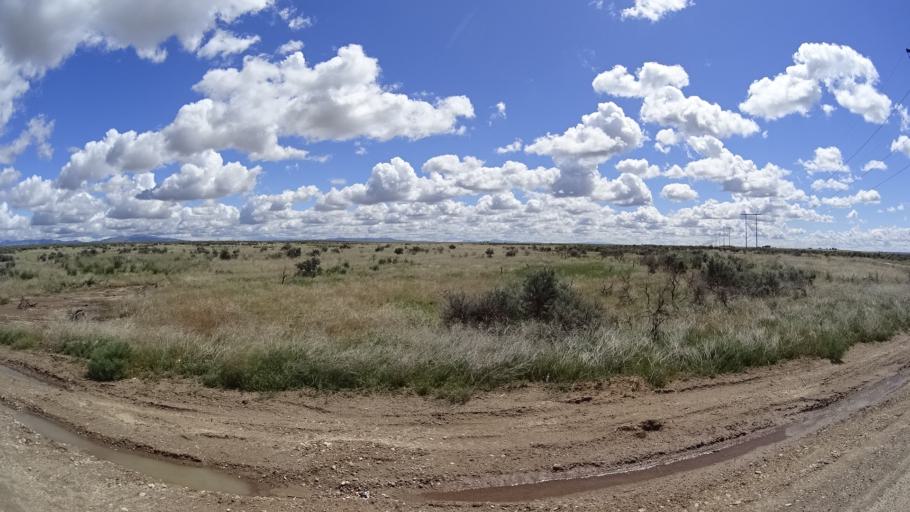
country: US
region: Idaho
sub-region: Ada County
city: Kuna
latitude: 43.4770
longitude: -116.2743
